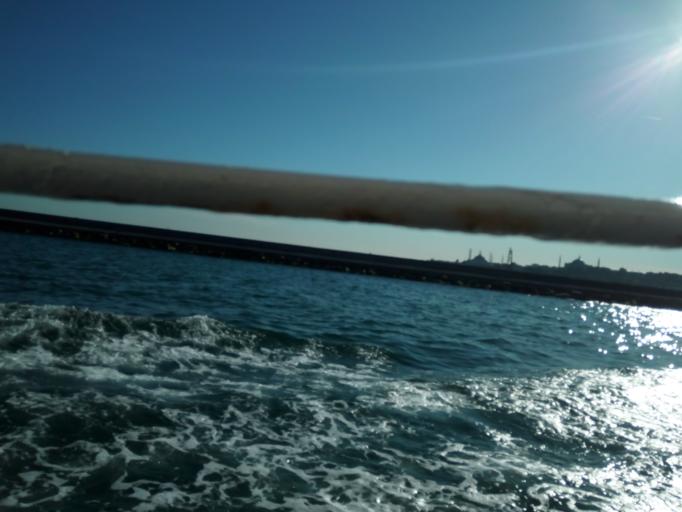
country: TR
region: Istanbul
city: UEskuedar
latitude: 41.0091
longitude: 29.0032
